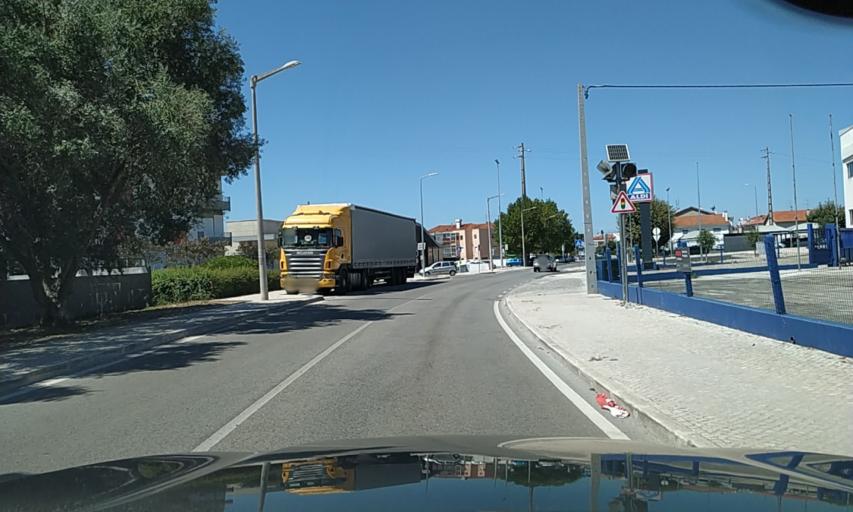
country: PT
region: Leiria
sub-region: Leiria
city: Leiria
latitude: 39.7600
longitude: -8.8212
